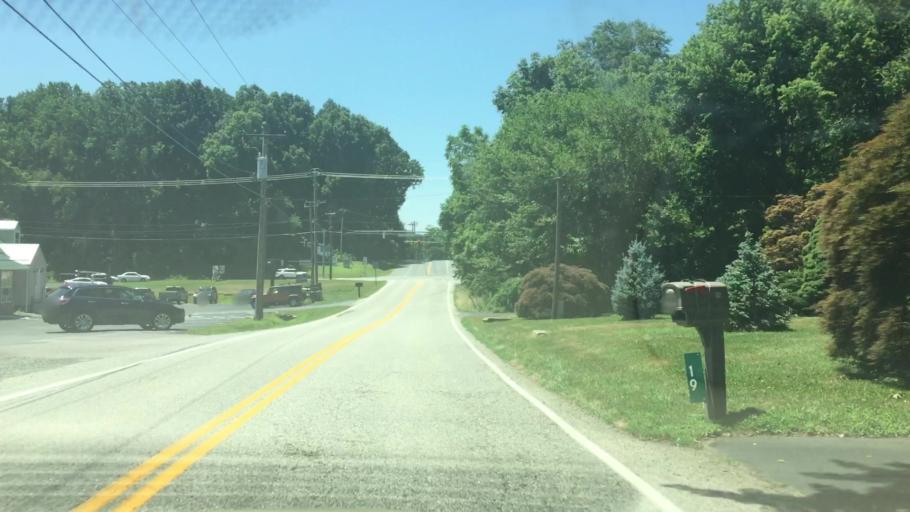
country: US
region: Maryland
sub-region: Cecil County
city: Rising Sun
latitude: 39.6745
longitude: -76.0721
